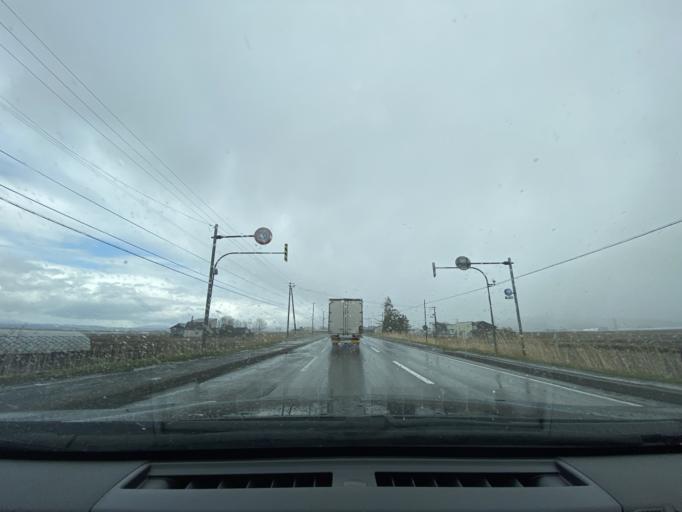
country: JP
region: Hokkaido
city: Fukagawa
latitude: 43.6586
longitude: 141.9870
